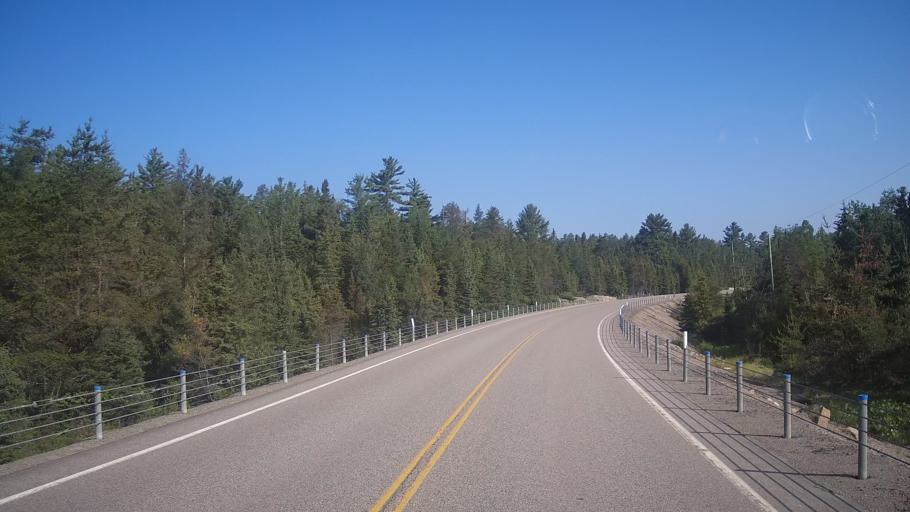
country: CA
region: Ontario
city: Rayside-Balfour
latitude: 46.7446
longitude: -81.6003
